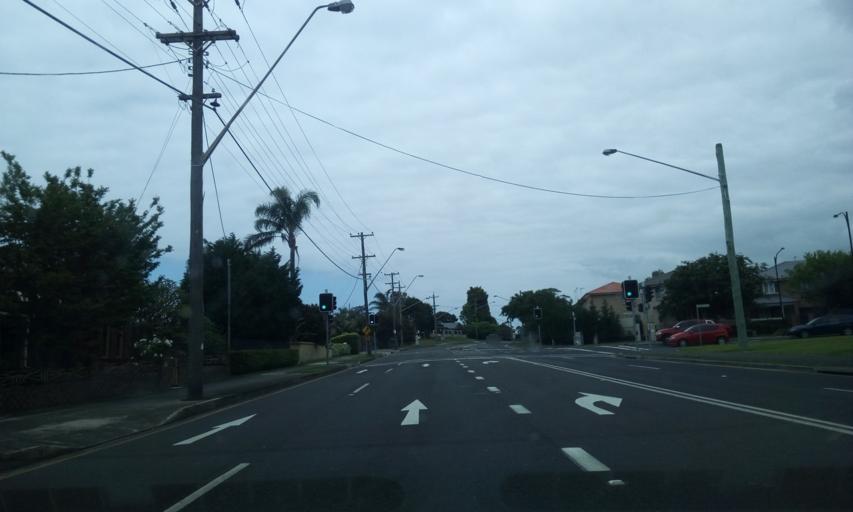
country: AU
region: New South Wales
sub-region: Wollongong
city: Bulli
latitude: -34.3479
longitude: 150.9039
